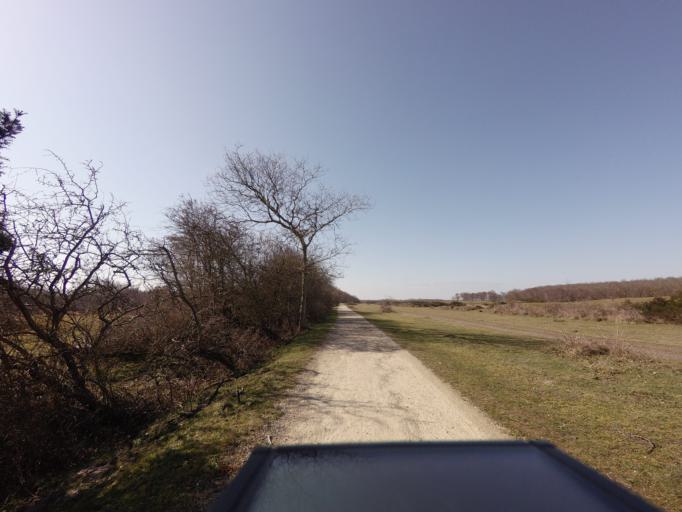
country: NL
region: Zeeland
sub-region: Schouwen-Duiveland
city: Renesse
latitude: 51.7260
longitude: 3.7625
